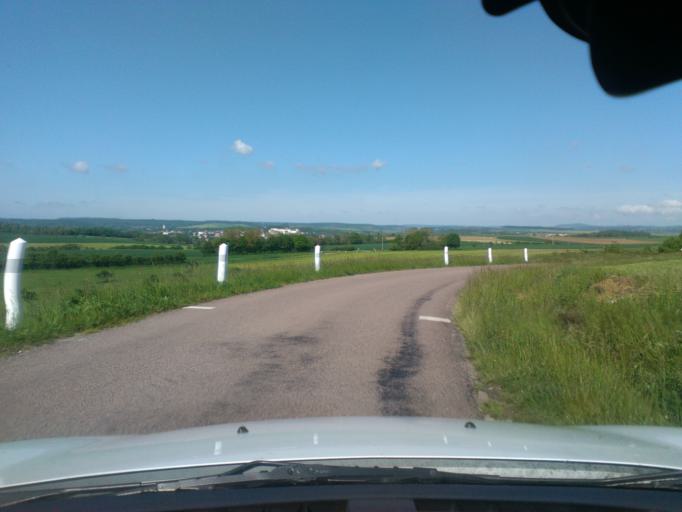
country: FR
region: Lorraine
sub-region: Departement des Vosges
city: Mirecourt
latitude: 48.3079
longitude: 6.1734
